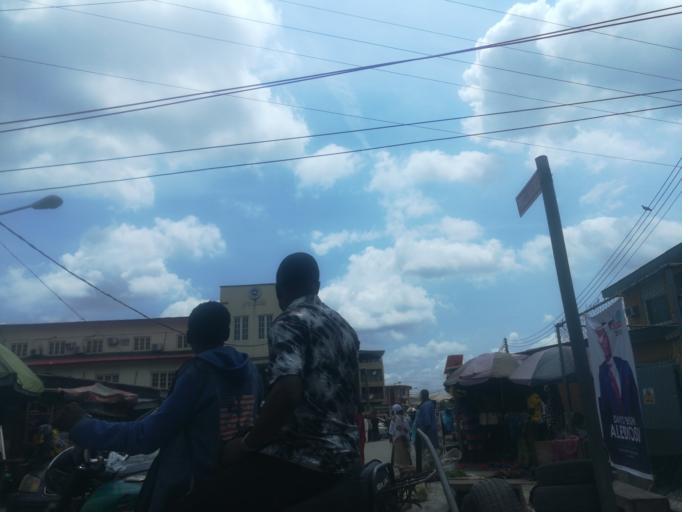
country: NG
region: Lagos
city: Somolu
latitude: 6.5574
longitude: 3.3865
